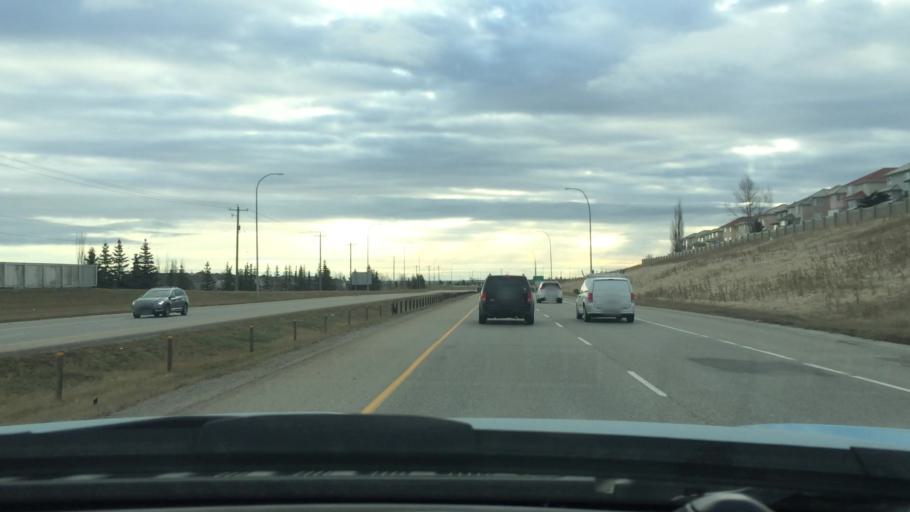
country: CA
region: Alberta
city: Calgary
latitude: 51.1462
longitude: -114.1321
